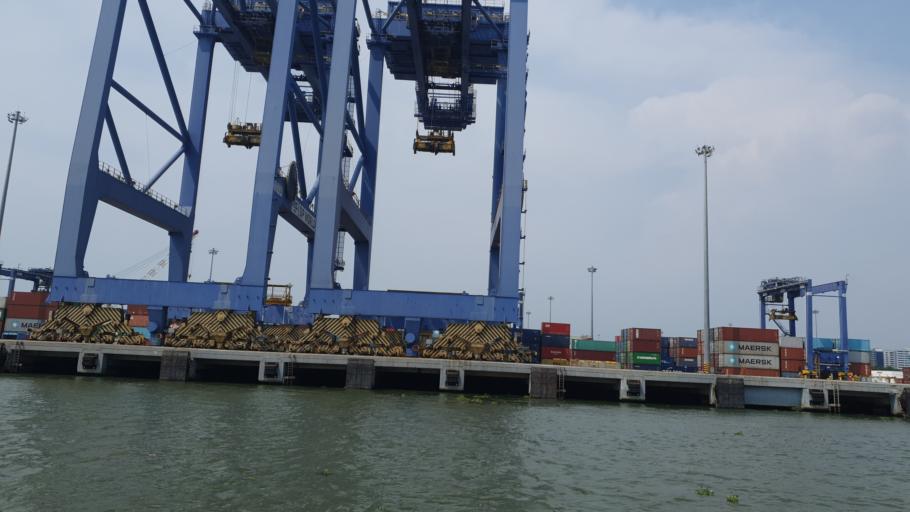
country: IN
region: Kerala
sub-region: Ernakulam
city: Cochin
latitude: 9.9766
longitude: 76.2514
